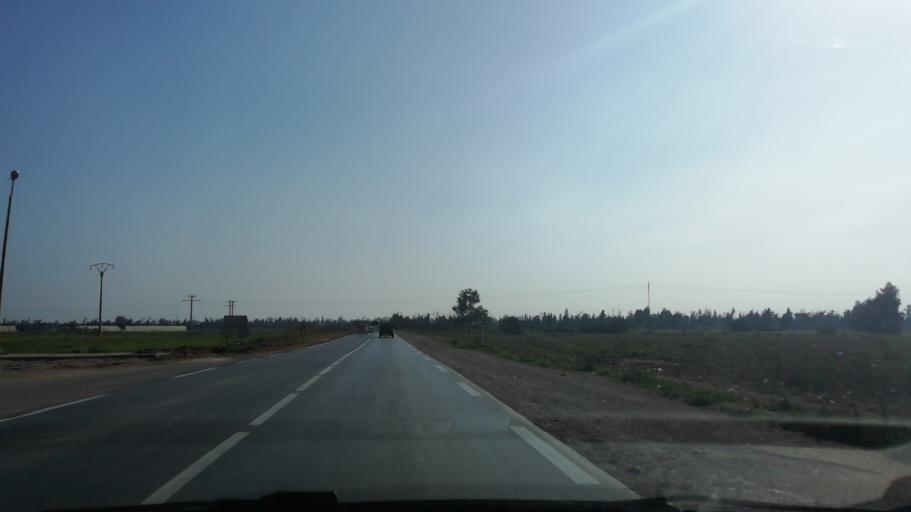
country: DZ
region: Mostaganem
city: Mostaganem
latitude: 35.7431
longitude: -0.0206
